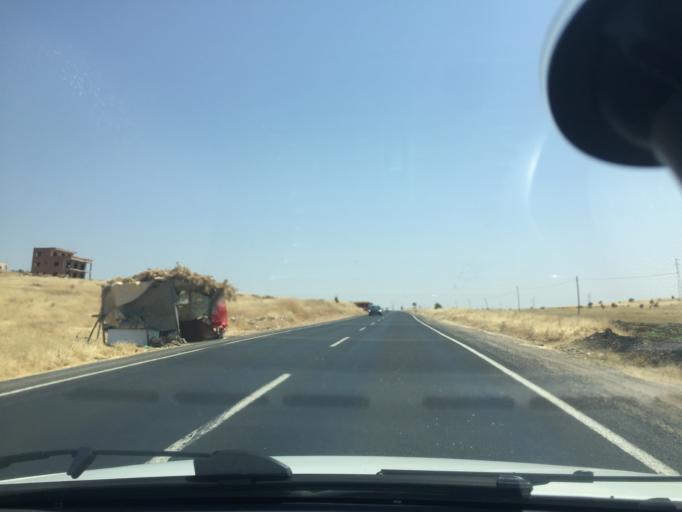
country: TR
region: Mardin
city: Acirli
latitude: 37.4429
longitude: 41.2879
